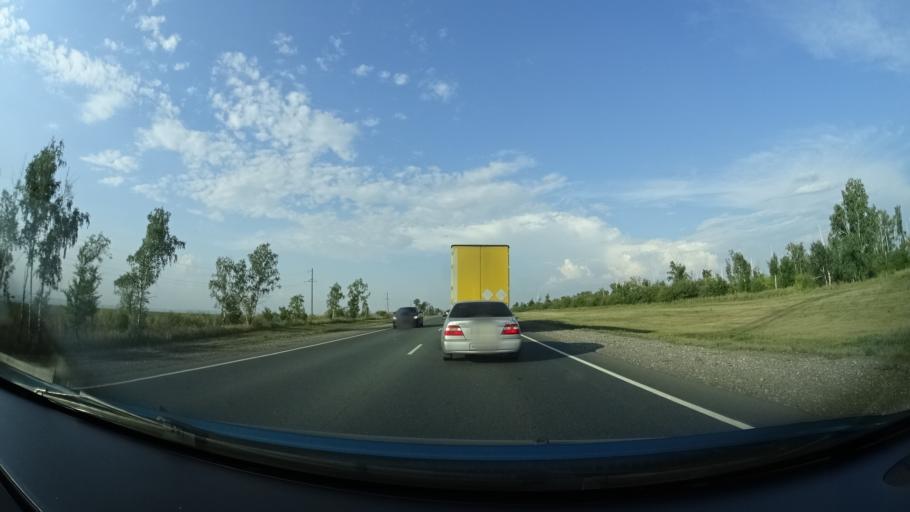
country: RU
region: Samara
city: Krasnyy Yar
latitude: 53.6705
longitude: 50.7662
